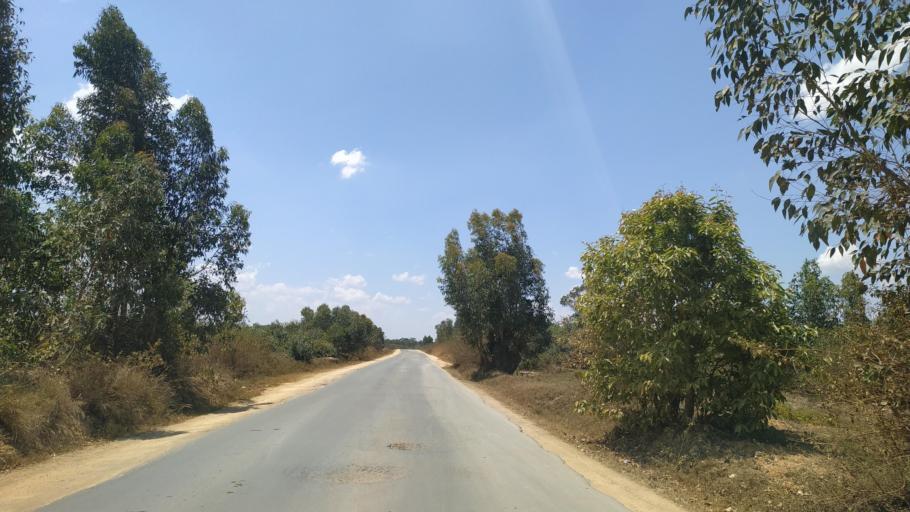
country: MG
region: Alaotra Mangoro
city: Ambatondrazaka
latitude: -18.2340
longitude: 48.2639
